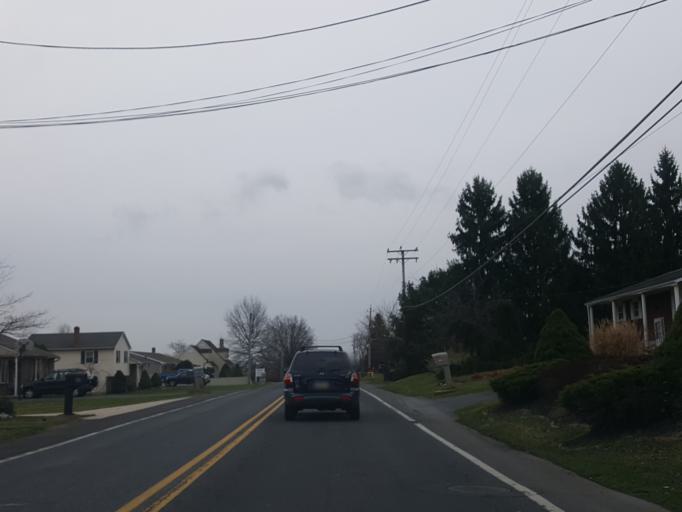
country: US
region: Pennsylvania
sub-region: Lebanon County
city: Lebanon
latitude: 40.3641
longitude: -76.4060
